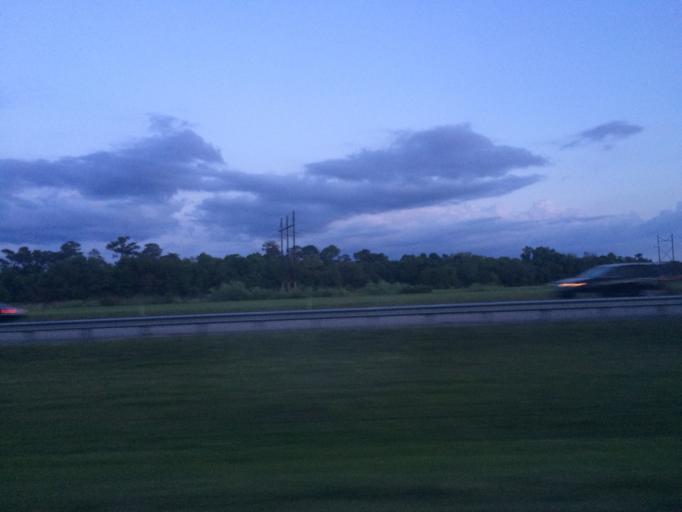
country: US
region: Florida
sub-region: Polk County
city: Loughman
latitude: 28.2657
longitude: -81.6087
